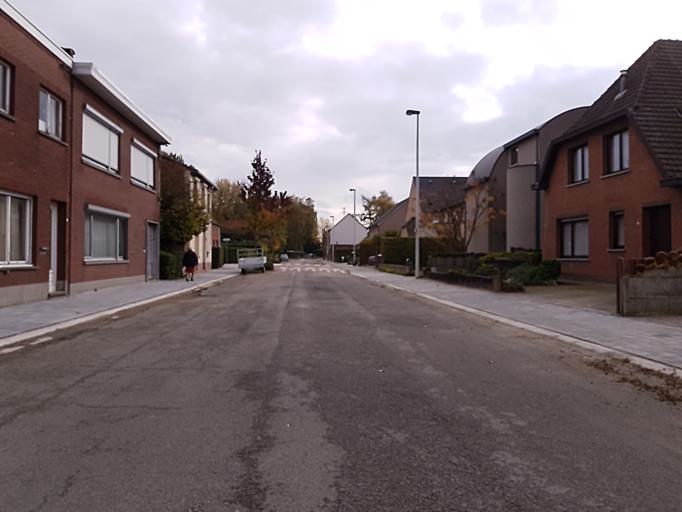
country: BE
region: Flanders
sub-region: Provincie Antwerpen
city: Ranst
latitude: 51.1859
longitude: 4.5665
